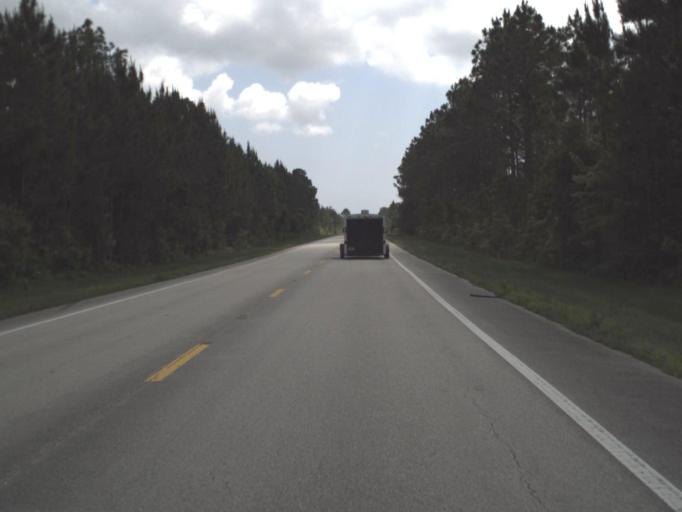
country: US
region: Florida
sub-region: Saint Johns County
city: Saint Augustine Shores
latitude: 29.7419
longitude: -81.3614
